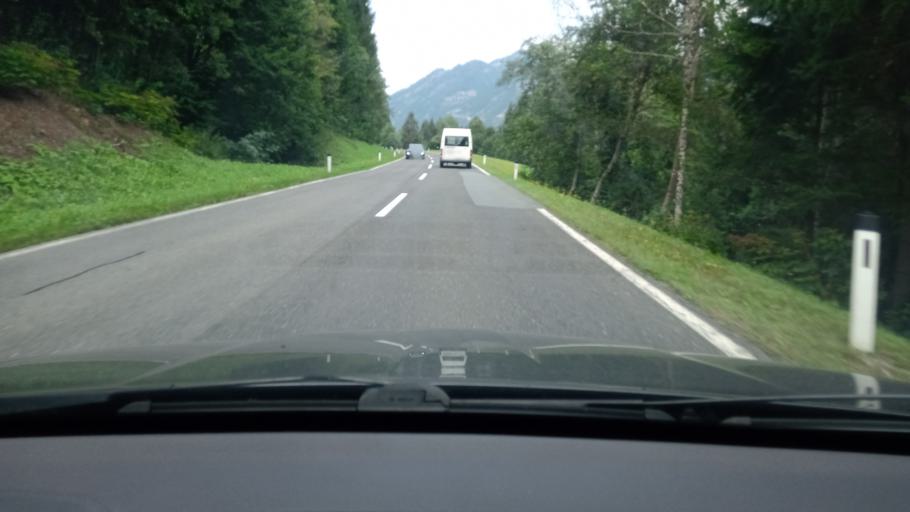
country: AT
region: Carinthia
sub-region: Politischer Bezirk Hermagor
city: Hermagor
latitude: 46.6506
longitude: 13.3283
